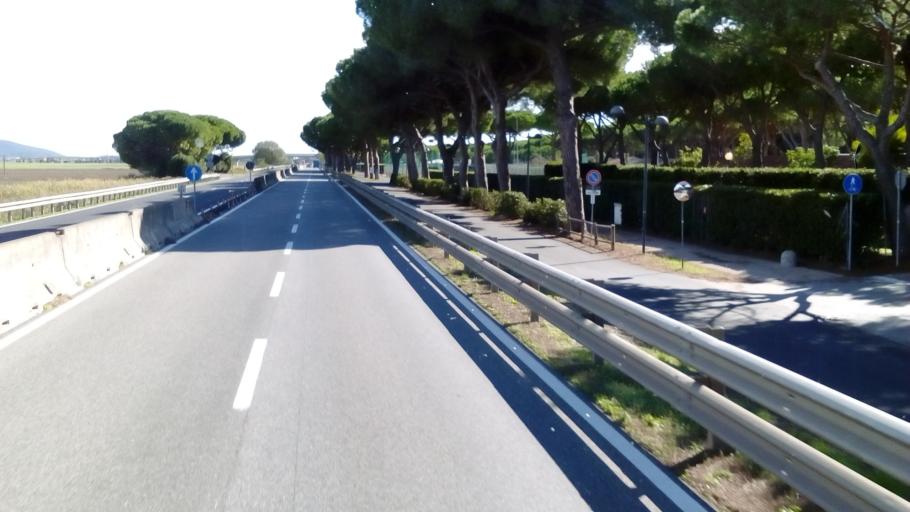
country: IT
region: Tuscany
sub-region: Provincia di Grosseto
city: Albinia
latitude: 42.5280
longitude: 11.1886
